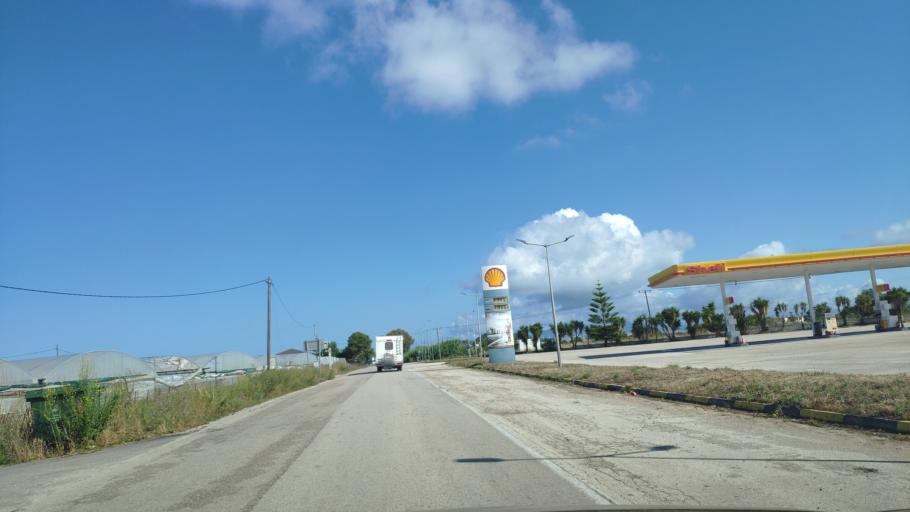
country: GR
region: Epirus
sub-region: Nomos Prevezis
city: Preveza
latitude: 38.9325
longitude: 20.7726
